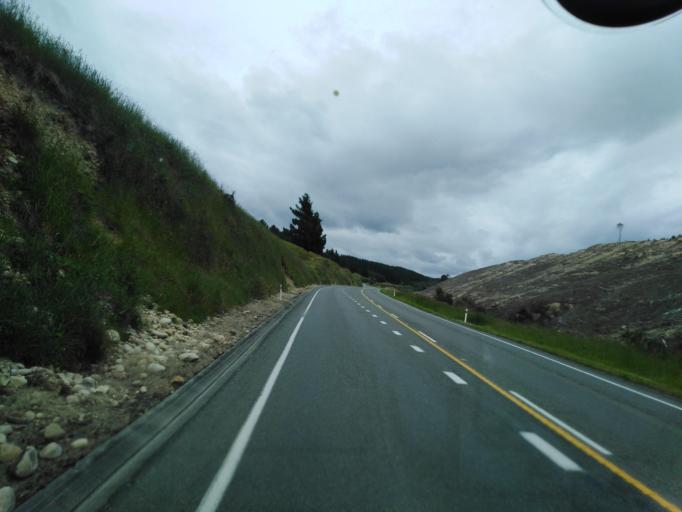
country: NZ
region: Tasman
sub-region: Tasman District
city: Wakefield
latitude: -41.4651
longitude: 172.9470
